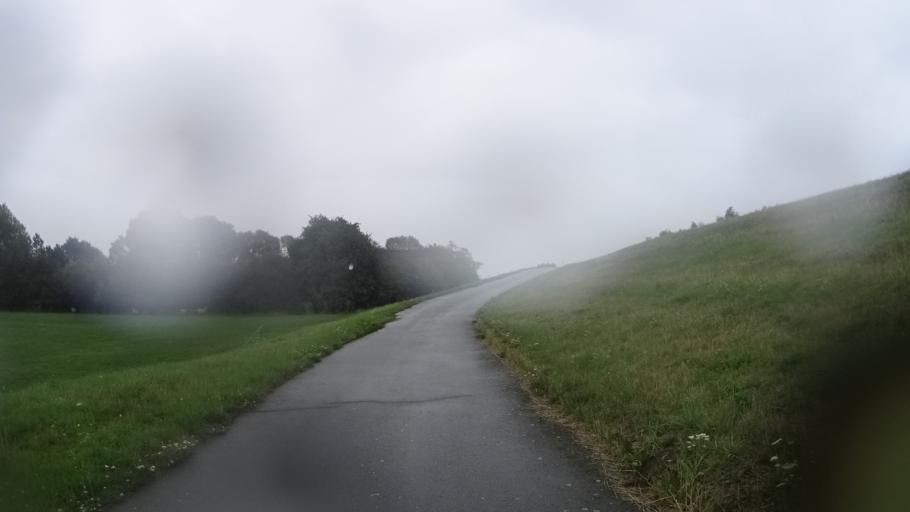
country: DE
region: Lower Saxony
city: Hitzacker
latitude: 53.1638
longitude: 11.0472
